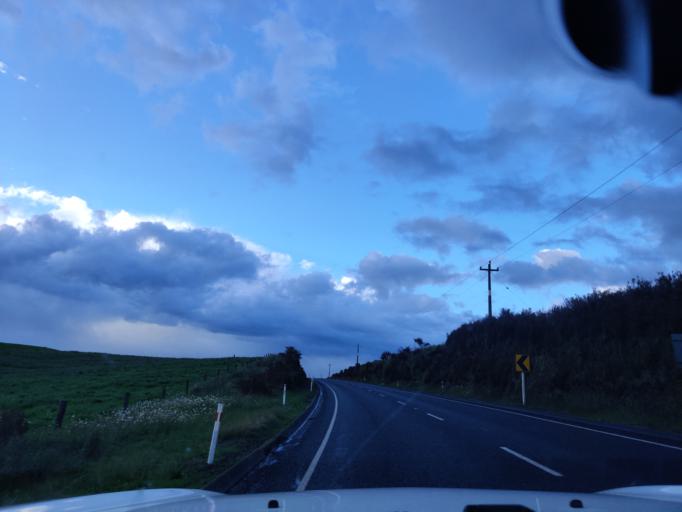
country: NZ
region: Waikato
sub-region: South Waikato District
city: Tokoroa
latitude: -38.3862
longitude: 175.7812
